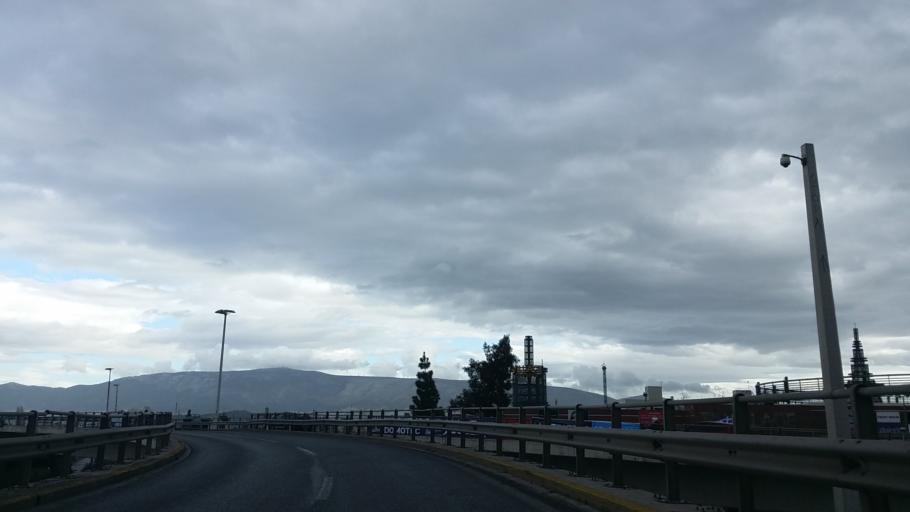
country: GR
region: Attica
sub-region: Nomos Piraios
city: Agios Ioannis Rentis
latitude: 37.9764
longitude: 23.6665
